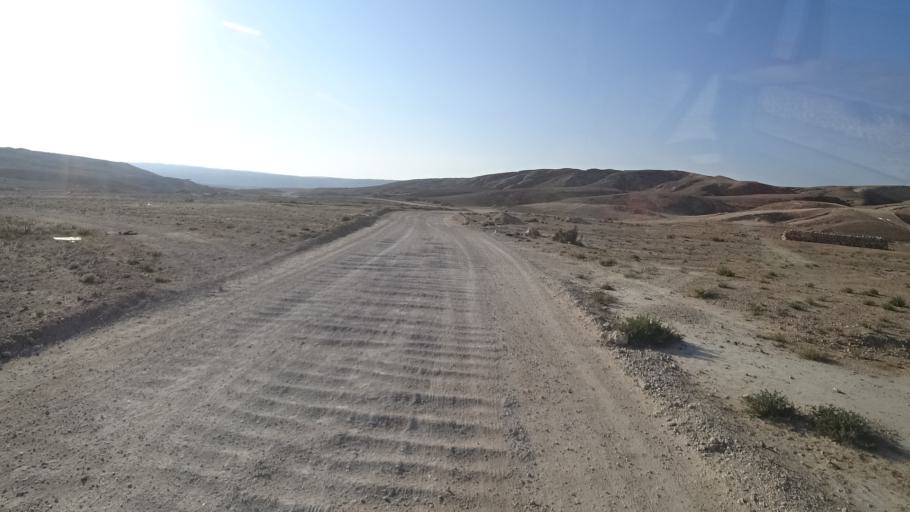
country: OM
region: Zufar
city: Salalah
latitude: 17.2420
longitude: 53.9145
